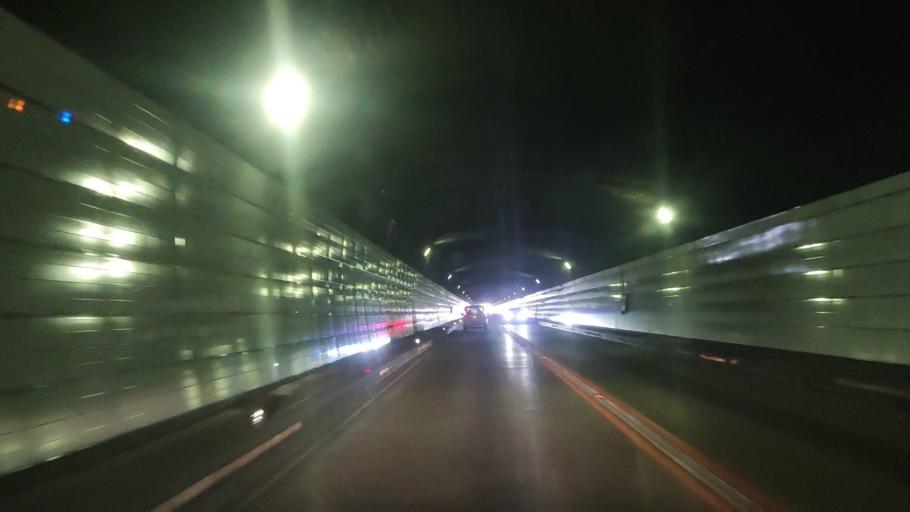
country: JP
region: Kumamoto
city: Hitoyoshi
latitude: 32.0930
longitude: 130.8024
